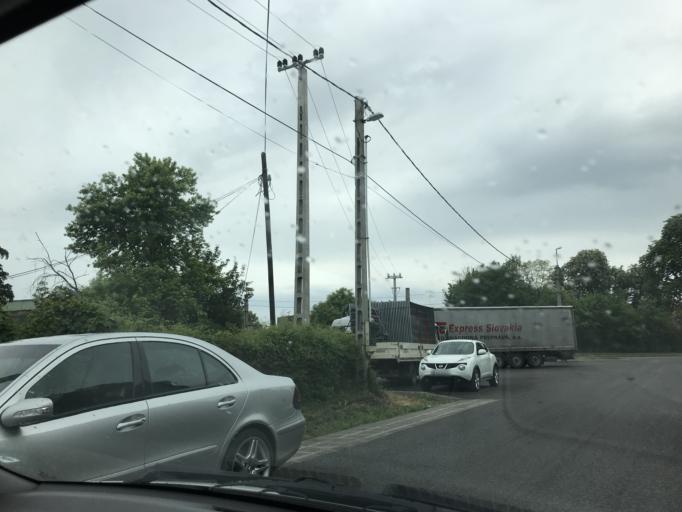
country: HU
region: Nograd
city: Batonyterenye
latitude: 47.9772
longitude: 19.8190
